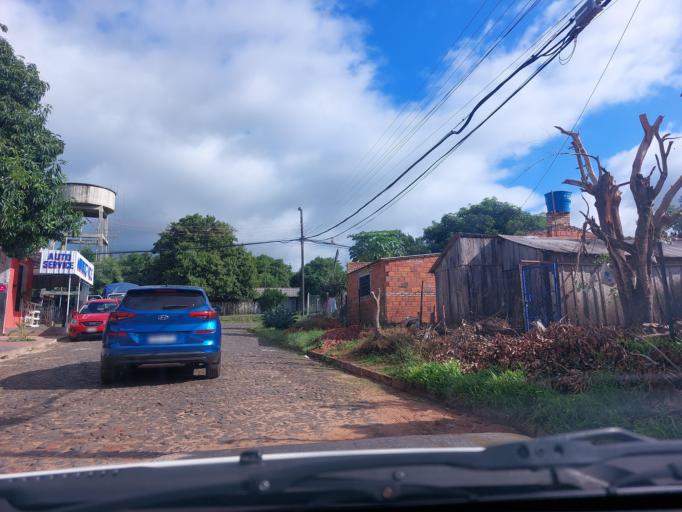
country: PY
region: San Pedro
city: Guayaybi
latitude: -24.6698
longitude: -56.4393
